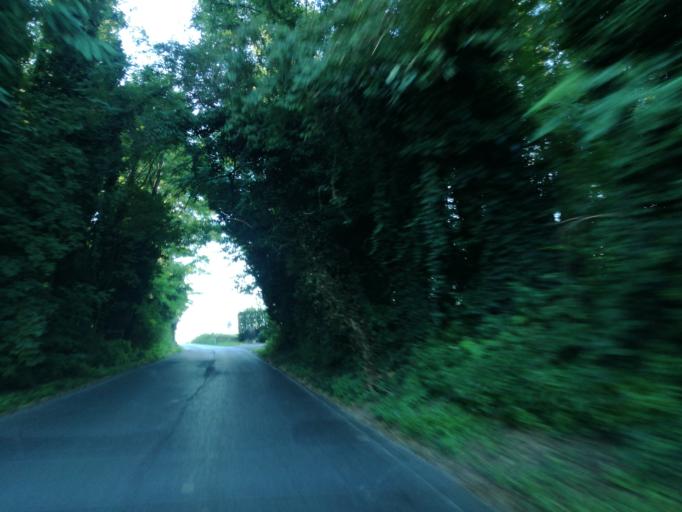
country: IT
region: Lombardy
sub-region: Provincia di Lecco
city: Verderio Inferiore
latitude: 45.6541
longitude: 9.4292
